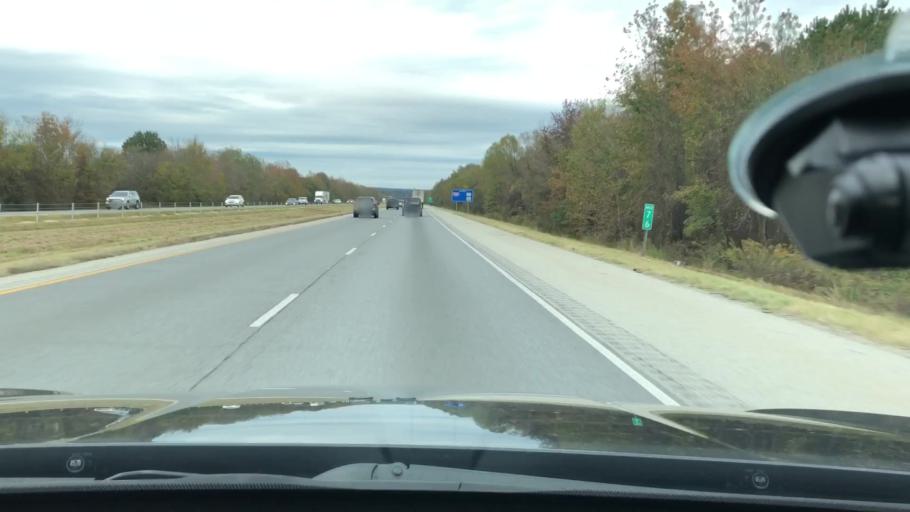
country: US
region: Arkansas
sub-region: Clark County
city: Arkadelphia
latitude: 34.1620
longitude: -93.0765
